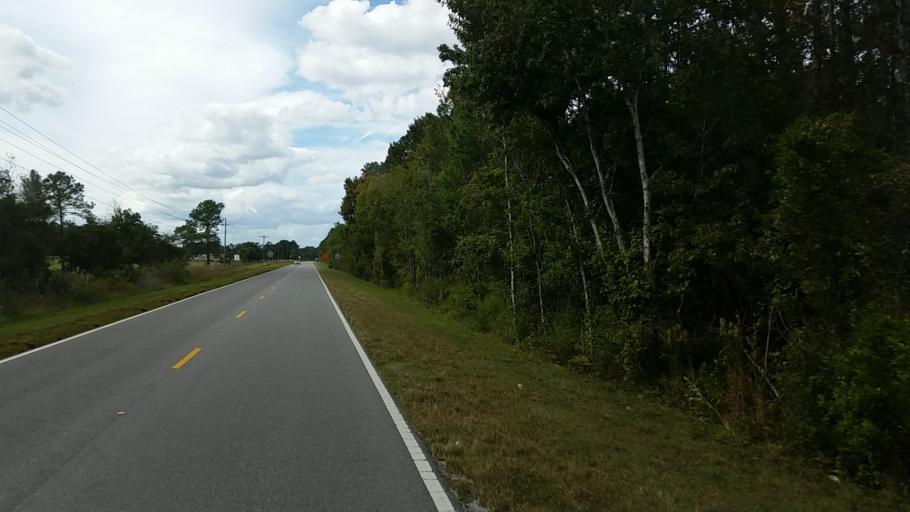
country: US
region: Florida
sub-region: Lake County
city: Four Corners
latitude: 28.3764
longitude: -81.8103
